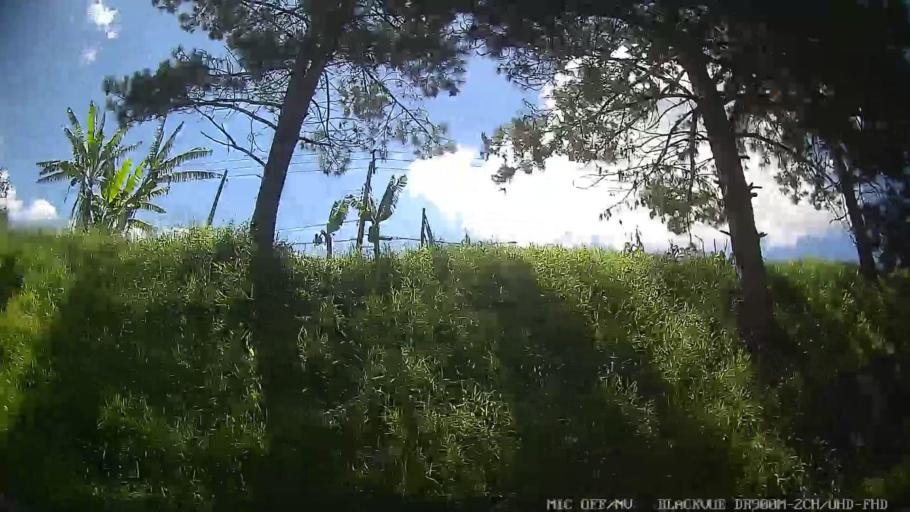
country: BR
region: Sao Paulo
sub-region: Mogi das Cruzes
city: Mogi das Cruzes
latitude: -23.6590
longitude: -46.2033
